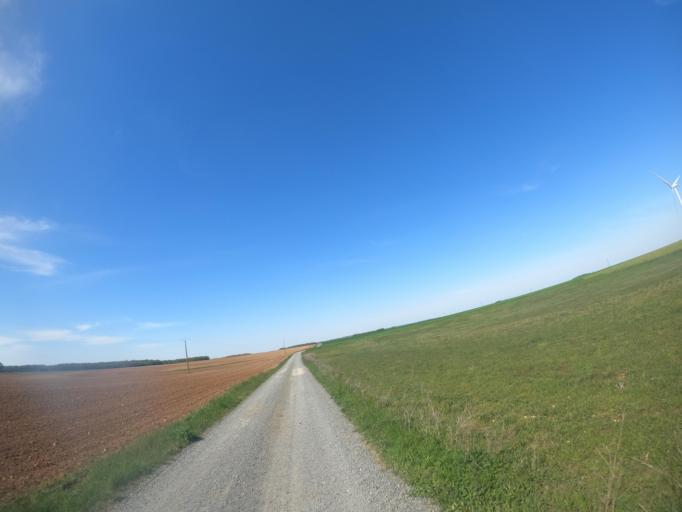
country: FR
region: Poitou-Charentes
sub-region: Departement des Deux-Sevres
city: Airvault
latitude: 46.8849
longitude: -0.1274
